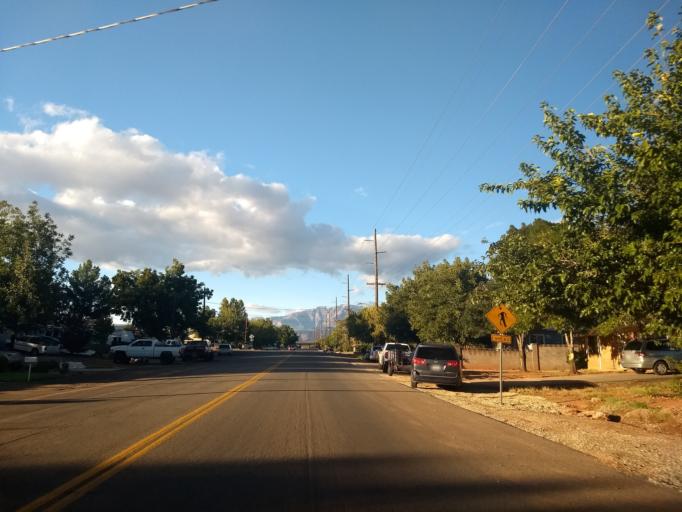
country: US
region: Utah
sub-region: Washington County
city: Washington
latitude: 37.1331
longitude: -113.5099
